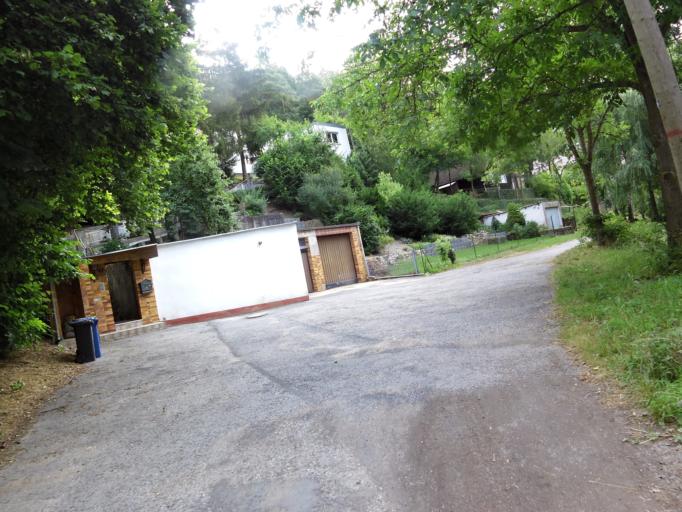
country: DE
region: Bavaria
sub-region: Regierungsbezirk Unterfranken
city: Reichenberg
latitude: 49.7514
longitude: 9.9449
